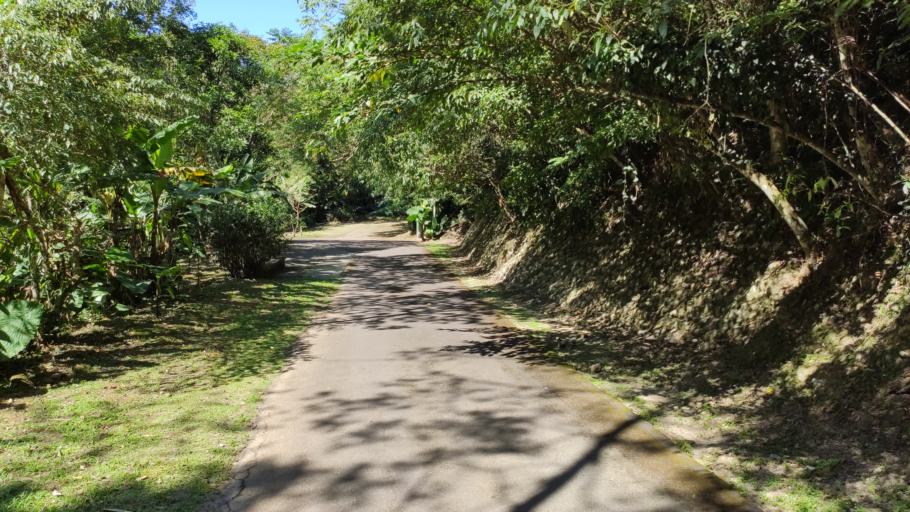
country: TW
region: Taiwan
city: Daxi
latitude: 24.8422
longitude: 121.3046
